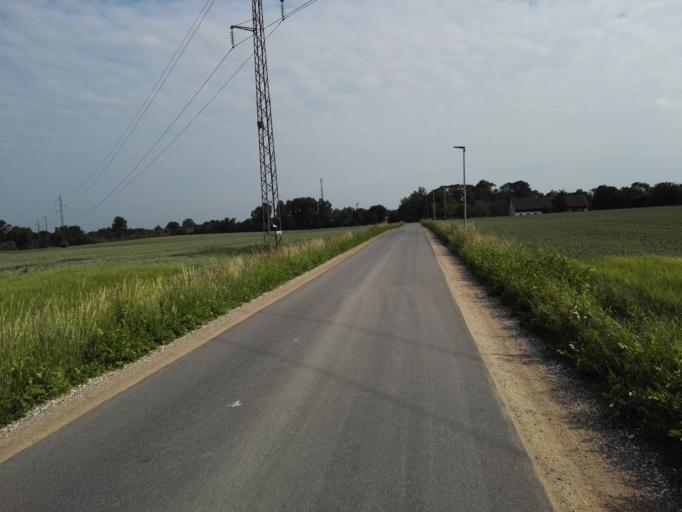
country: DK
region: Capital Region
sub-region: Egedal Kommune
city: Olstykke
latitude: 55.7739
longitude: 12.1381
